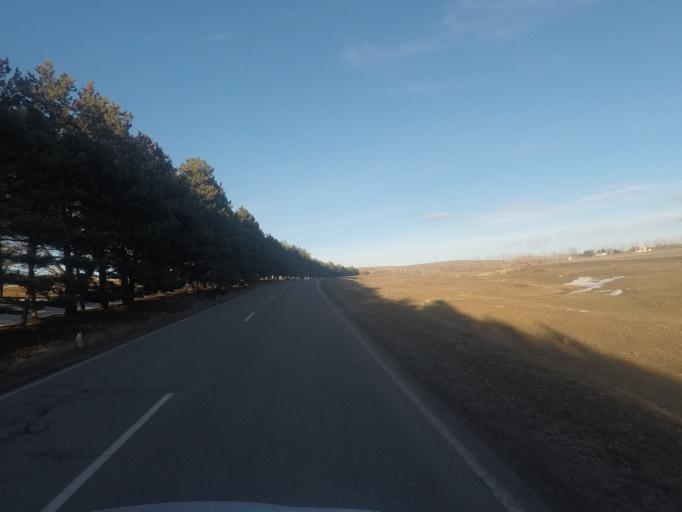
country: GE
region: Kvemo Kartli
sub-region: Tsalka
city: Tsalka
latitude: 41.6141
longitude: 44.1266
